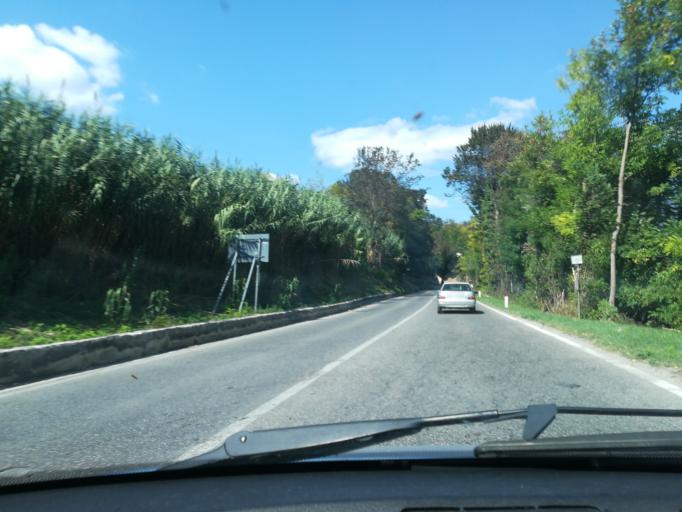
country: IT
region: The Marches
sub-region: Provincia di Macerata
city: Sforzacosta
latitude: 43.2765
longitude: 13.4314
